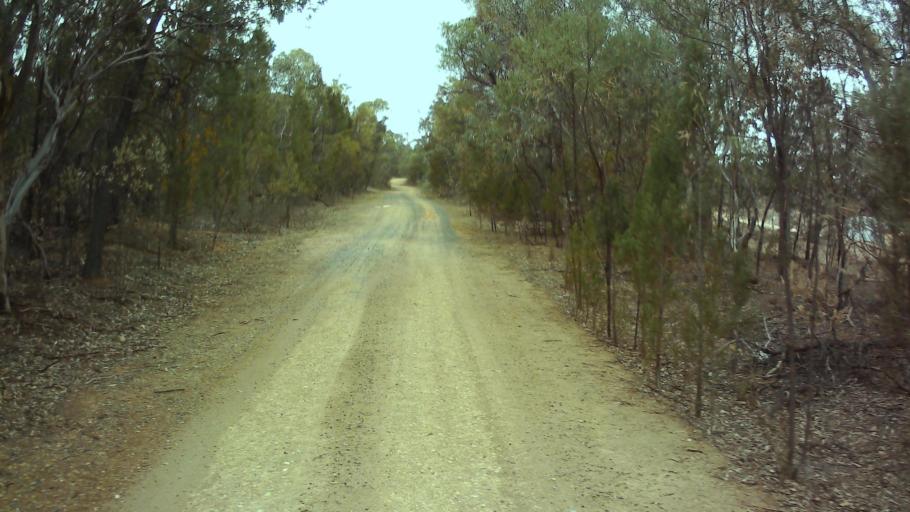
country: AU
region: New South Wales
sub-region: Weddin
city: Grenfell
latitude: -33.8870
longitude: 148.1573
